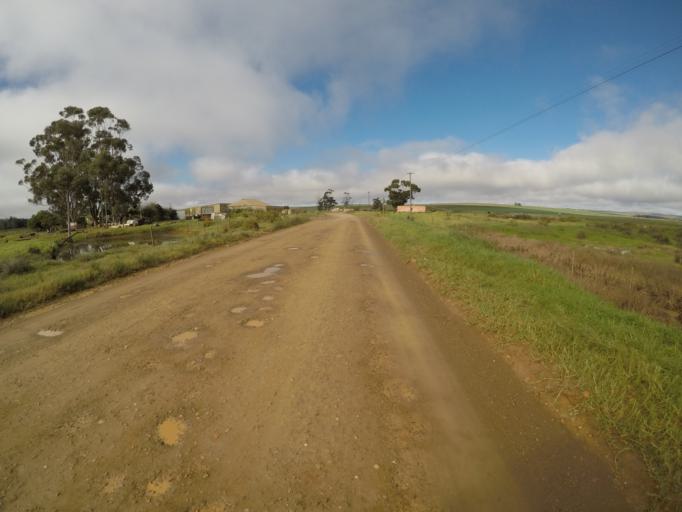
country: ZA
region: Western Cape
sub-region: Cape Winelands District Municipality
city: Ashton
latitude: -34.1456
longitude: 19.8676
